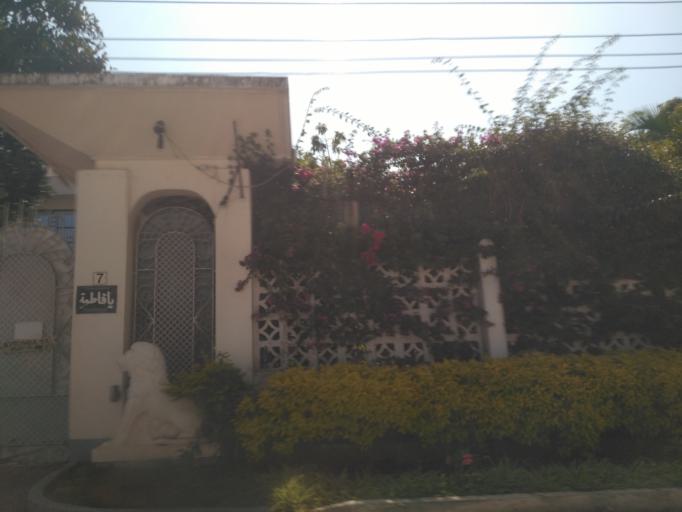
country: TZ
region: Dar es Salaam
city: Dar es Salaam
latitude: -6.8035
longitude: 39.2823
